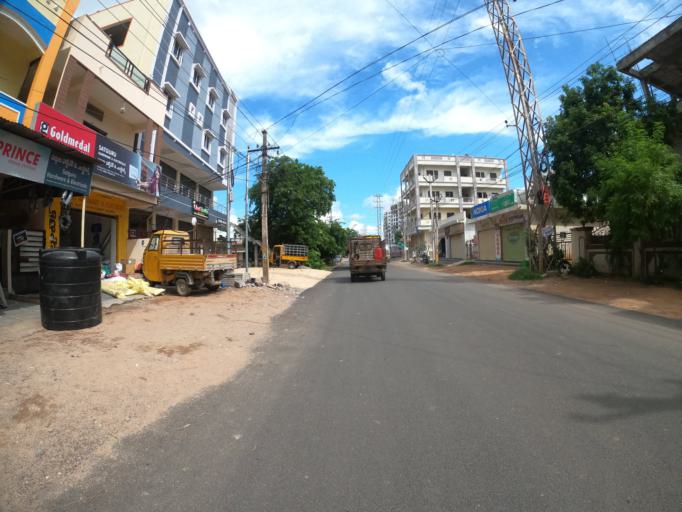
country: IN
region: Telangana
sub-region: Hyderabad
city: Hyderabad
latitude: 17.3528
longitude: 78.3895
